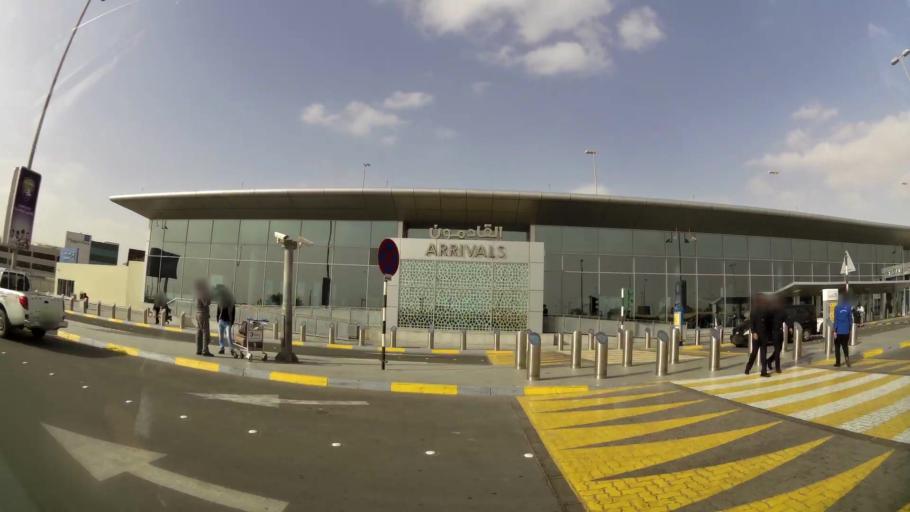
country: AE
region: Abu Dhabi
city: Abu Dhabi
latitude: 24.4264
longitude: 54.6447
